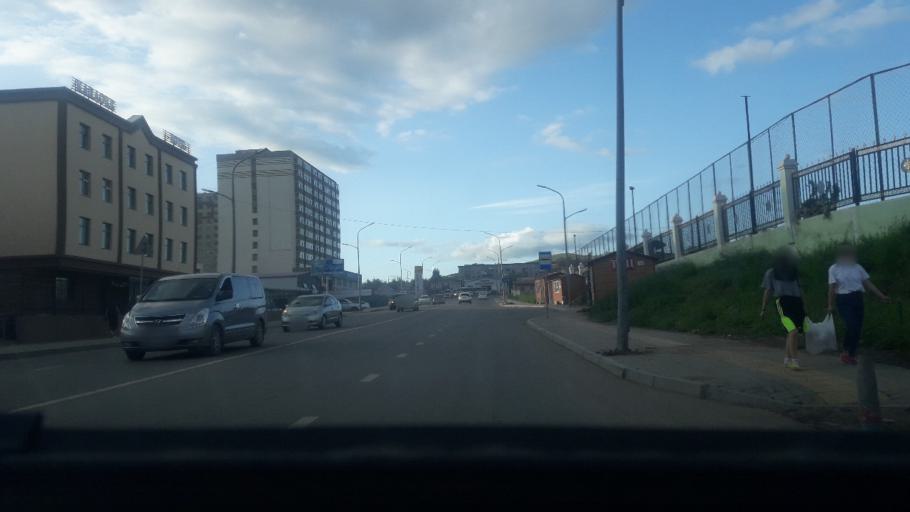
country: MN
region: Ulaanbaatar
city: Ulaanbaatar
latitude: 47.9214
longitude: 106.9859
